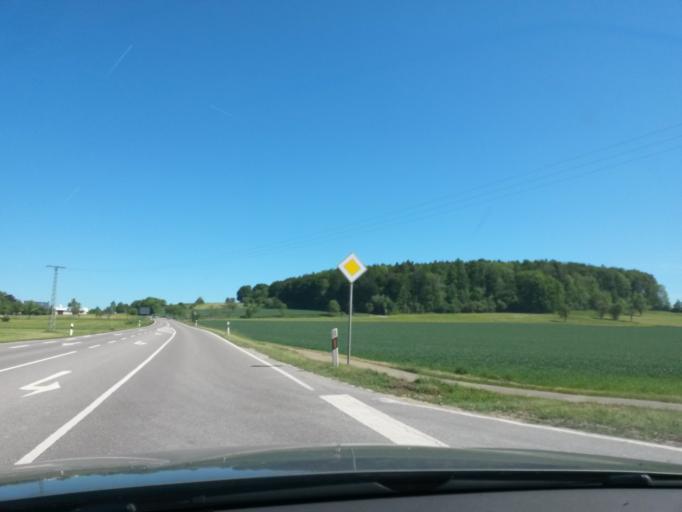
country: DE
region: Baden-Wuerttemberg
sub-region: Tuebingen Region
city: Trochtelfingen
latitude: 48.2661
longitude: 9.2799
